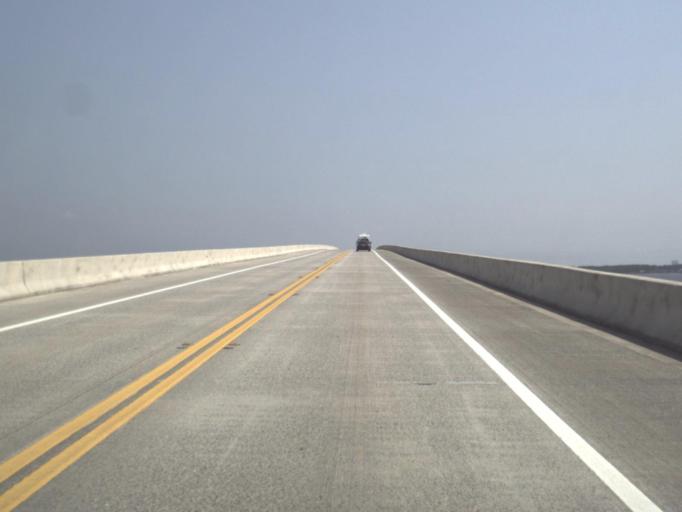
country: US
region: Florida
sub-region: Santa Rosa County
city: Oriole Beach
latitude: 30.4206
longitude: -87.0905
